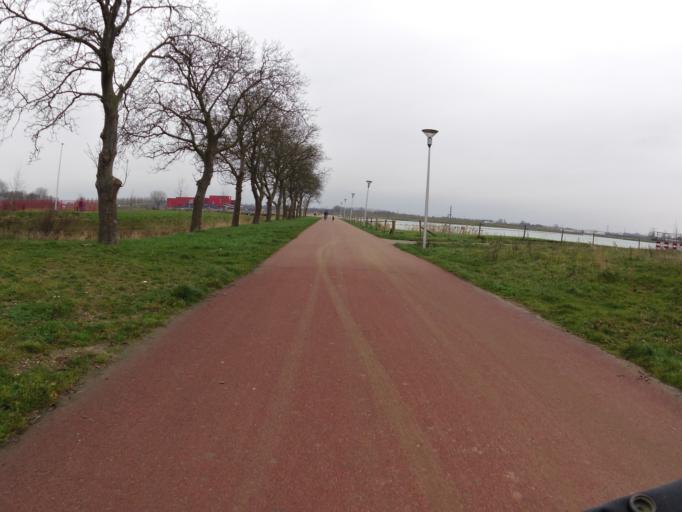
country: NL
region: Gelderland
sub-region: Gemeente Nijmegen
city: Nijmegen
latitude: 51.8744
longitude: 5.8633
